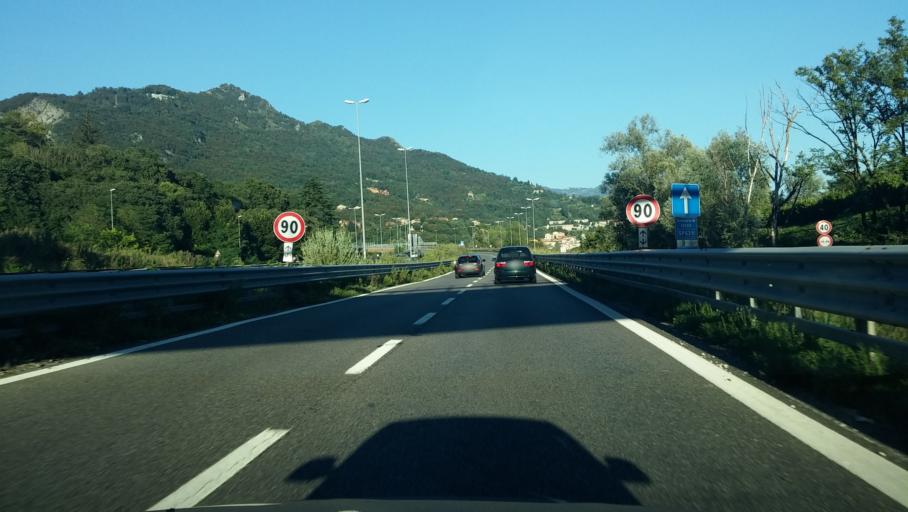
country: IT
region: Lombardy
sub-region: Provincia di Lecco
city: Civate
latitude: 45.8244
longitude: 9.3438
